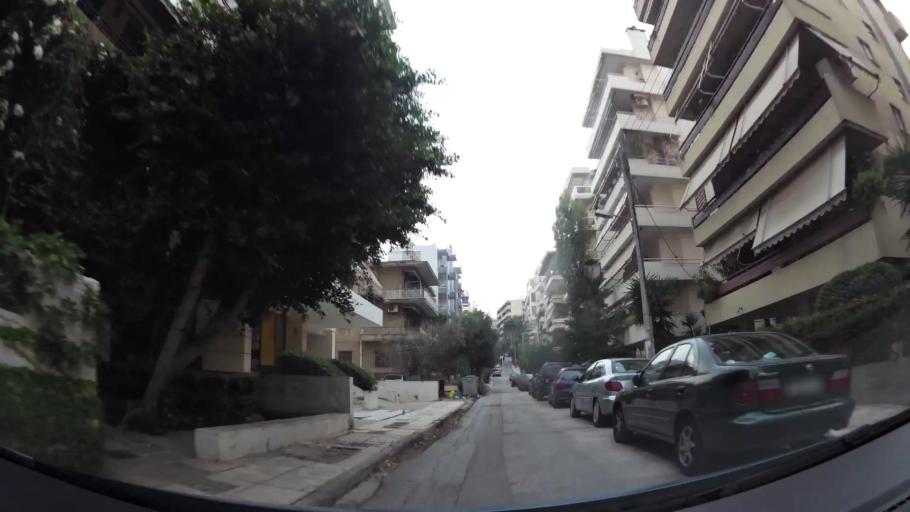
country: GR
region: Attica
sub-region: Nomarchia Athinas
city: Palaio Faliro
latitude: 37.9202
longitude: 23.7037
